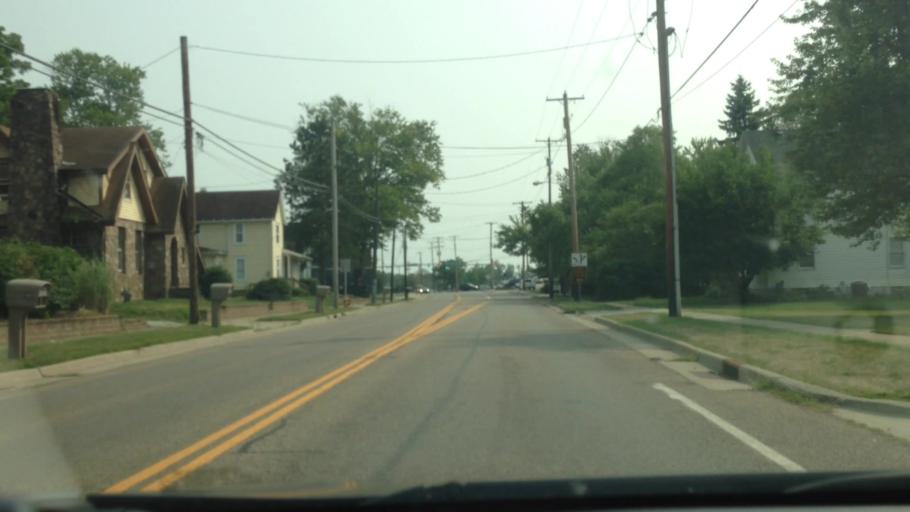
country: US
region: Ohio
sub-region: Summit County
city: Greensburg
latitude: 40.9334
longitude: -81.4650
